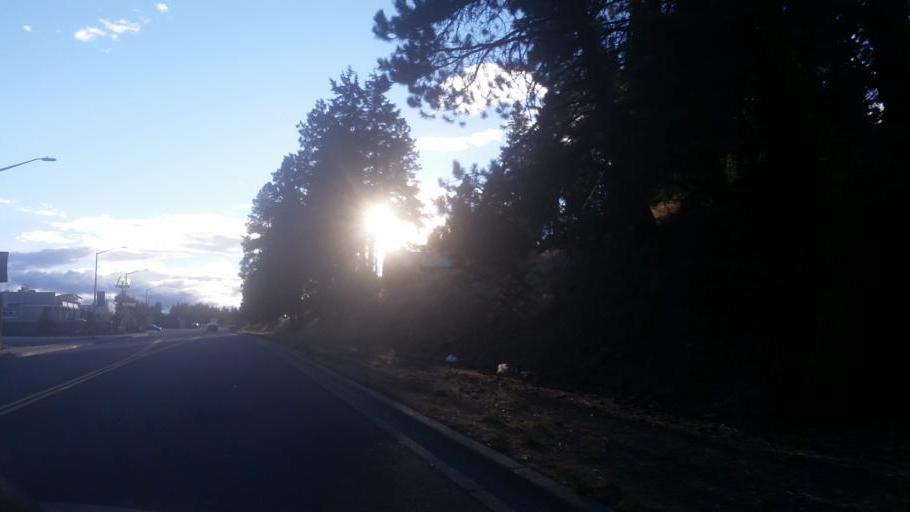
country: US
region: Washington
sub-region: Kittitas County
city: Cle Elum
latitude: 47.1962
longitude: -120.9502
